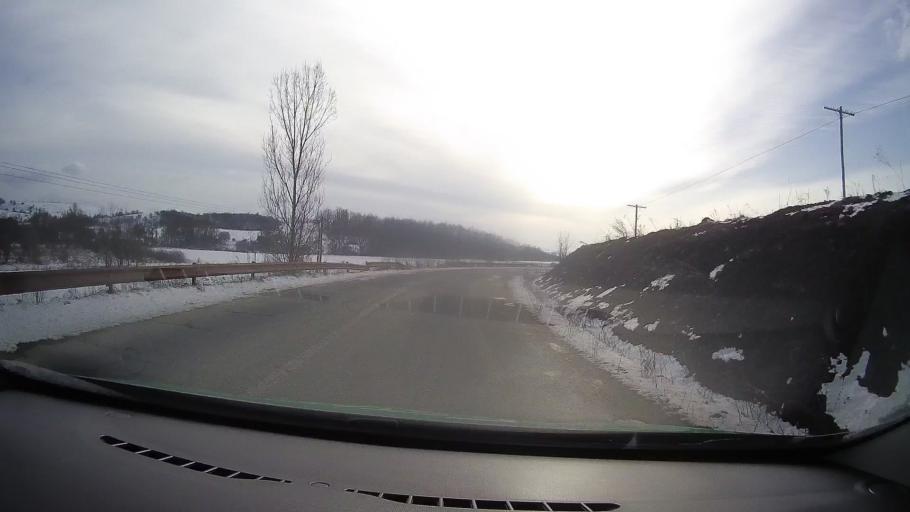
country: RO
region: Sibiu
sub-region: Comuna Iacobeni
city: Iacobeni
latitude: 46.0170
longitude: 24.6952
